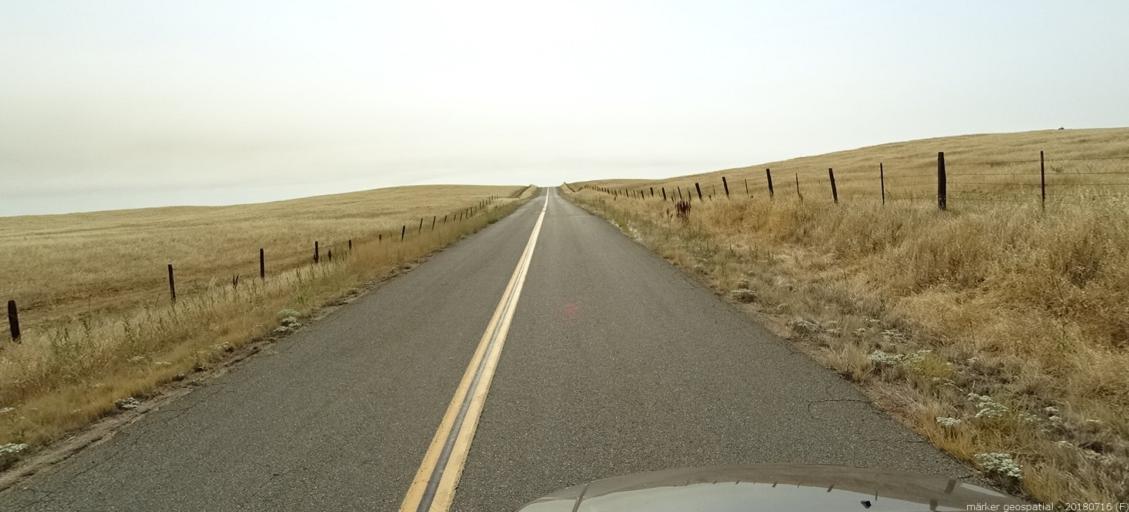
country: US
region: California
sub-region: Madera County
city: Madera Acres
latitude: 37.1194
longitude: -119.9781
